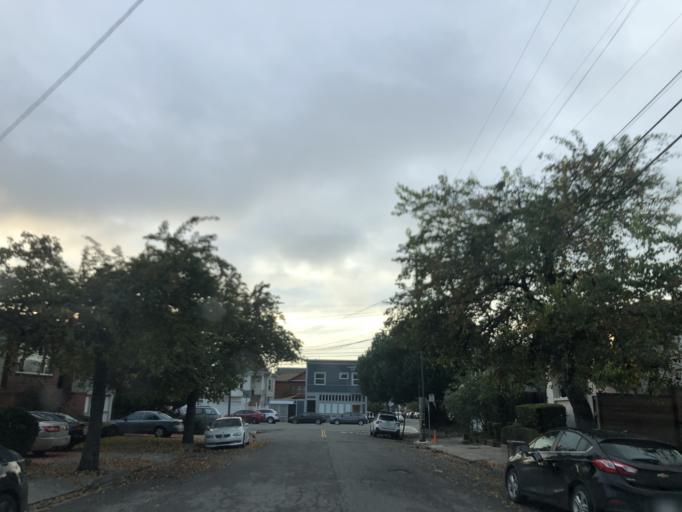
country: US
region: California
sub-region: Alameda County
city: Emeryville
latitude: 37.8436
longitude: -122.2642
